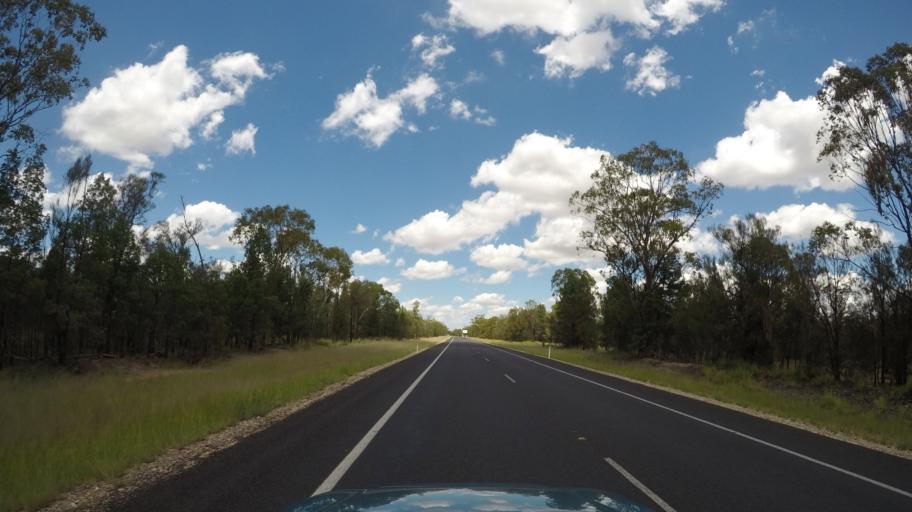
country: AU
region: Queensland
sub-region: Goondiwindi
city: Goondiwindi
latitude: -28.0687
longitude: 150.7543
